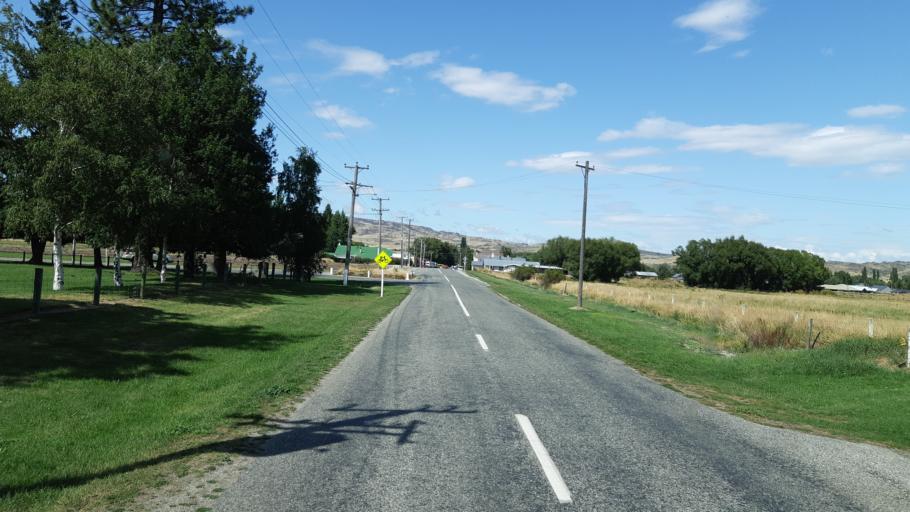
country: NZ
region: Otago
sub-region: Queenstown-Lakes District
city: Wanaka
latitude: -45.0910
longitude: 169.6019
